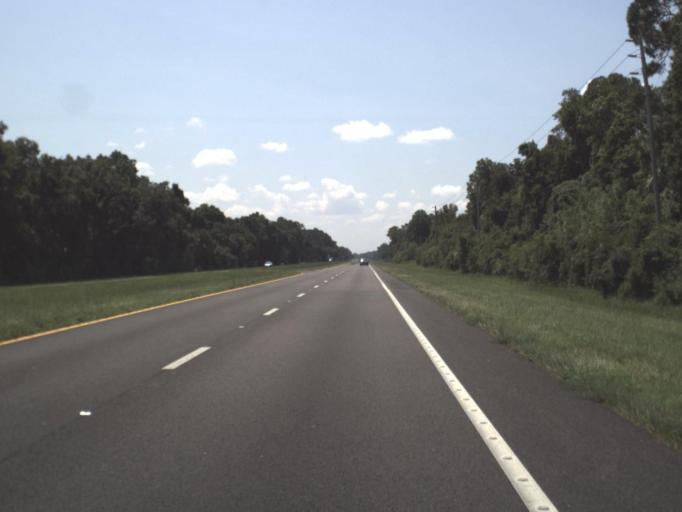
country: US
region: Florida
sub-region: Citrus County
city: Crystal River
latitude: 28.9332
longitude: -82.6173
